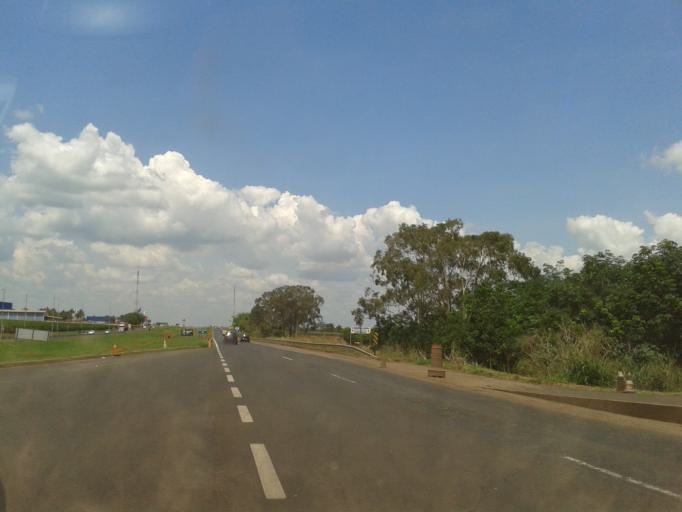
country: BR
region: Minas Gerais
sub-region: Araguari
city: Araguari
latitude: -18.6935
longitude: -48.1819
